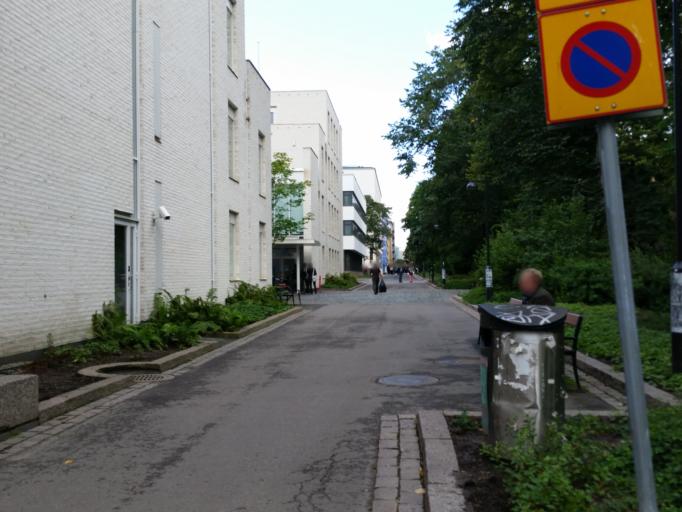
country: FI
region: Uusimaa
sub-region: Helsinki
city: Helsinki
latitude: 60.1732
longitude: 24.9532
